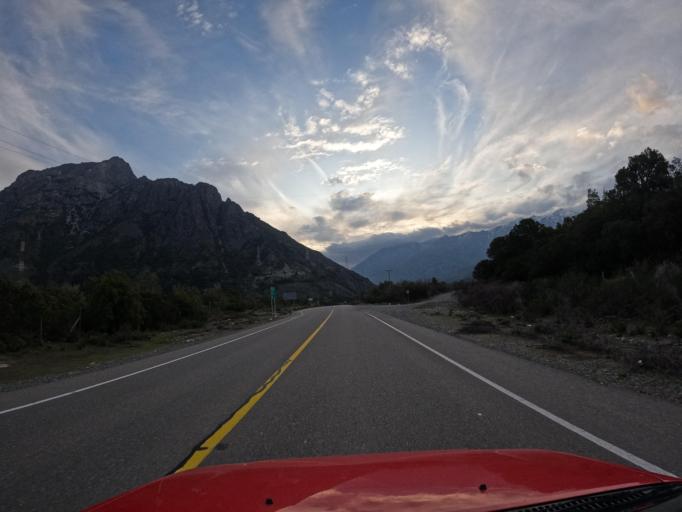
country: CL
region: Maule
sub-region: Provincia de Linares
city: Colbun
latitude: -35.7103
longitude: -71.0704
